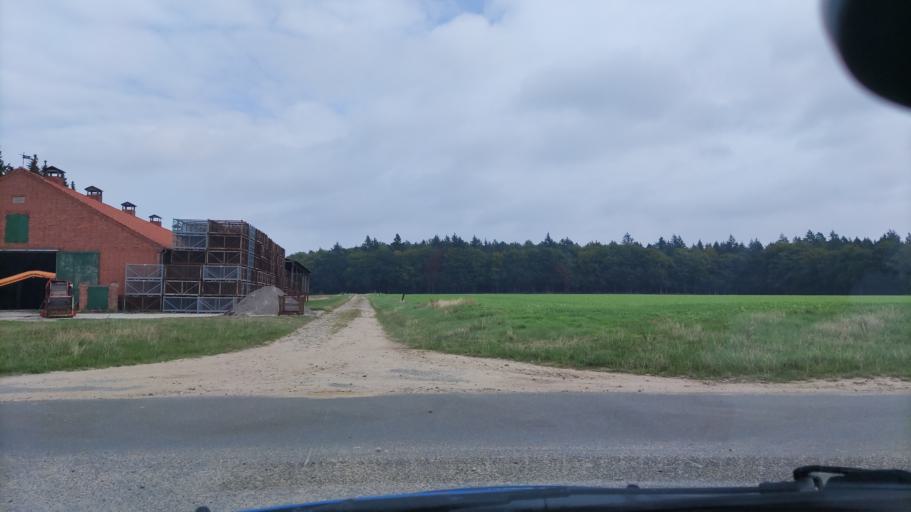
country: DE
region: Lower Saxony
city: Altenmedingen
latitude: 53.1577
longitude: 10.5715
